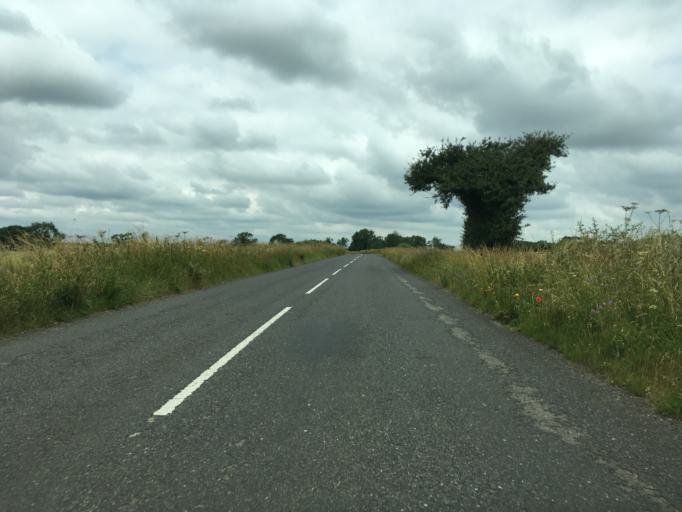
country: GB
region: England
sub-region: Oxfordshire
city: Charlbury
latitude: 51.9110
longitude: -1.4901
